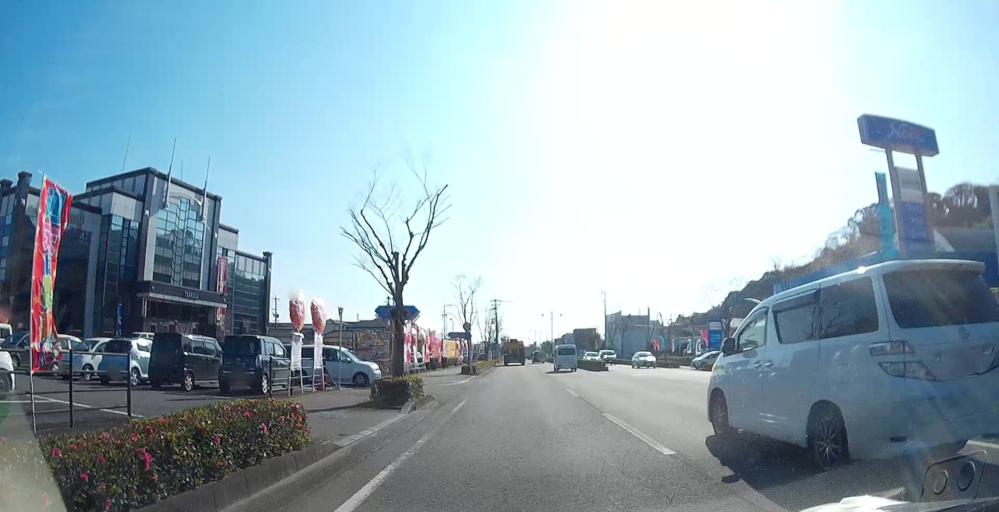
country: JP
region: Kumamoto
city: Kumamoto
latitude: 32.7874
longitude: 130.6734
